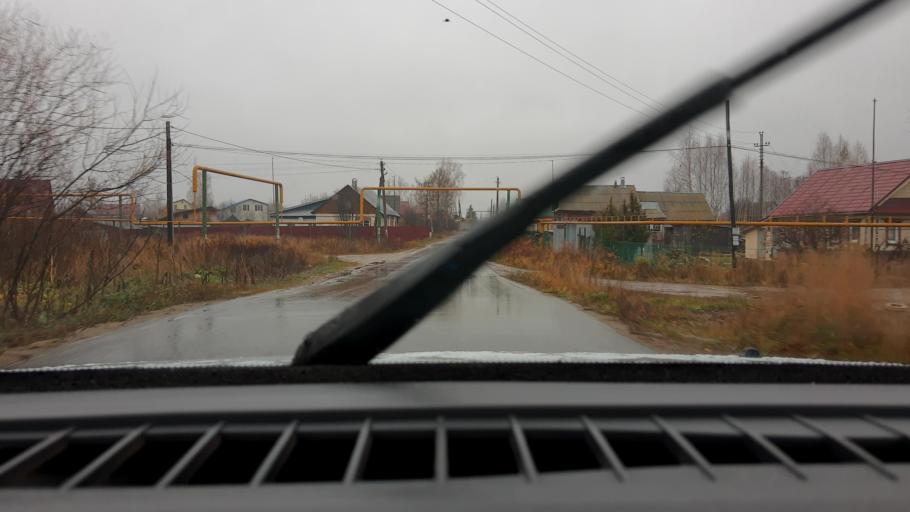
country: RU
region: Nizjnij Novgorod
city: Linda
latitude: 56.6794
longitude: 44.1960
